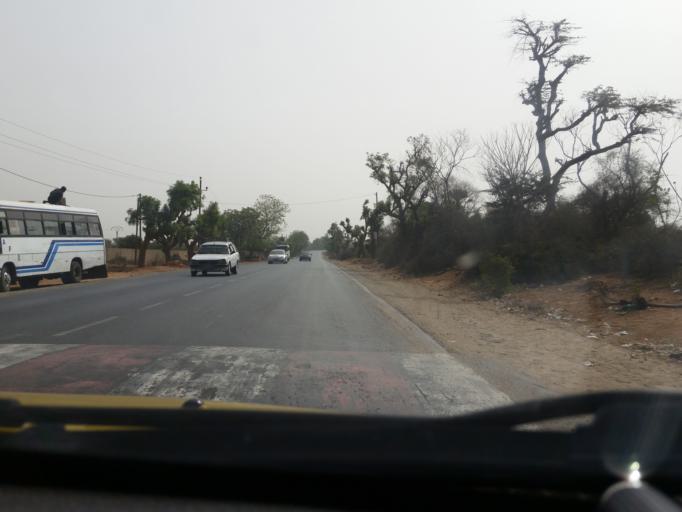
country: SN
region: Thies
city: Pout
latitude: 14.7535
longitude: -17.1263
